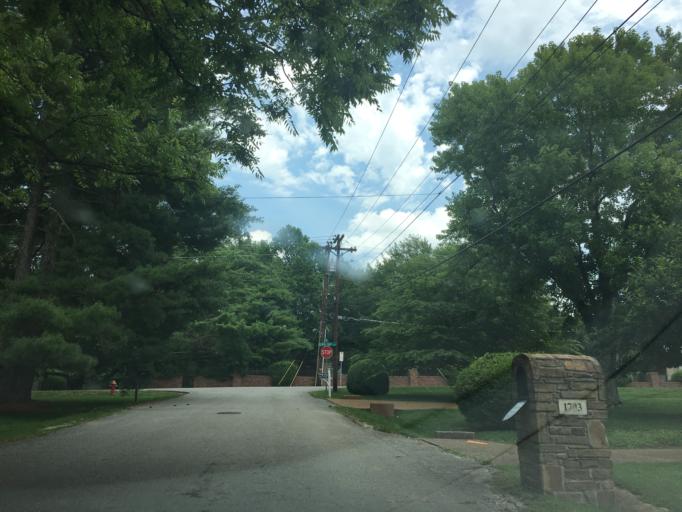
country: US
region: Tennessee
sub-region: Davidson County
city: Oak Hill
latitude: 36.0990
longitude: -86.8060
